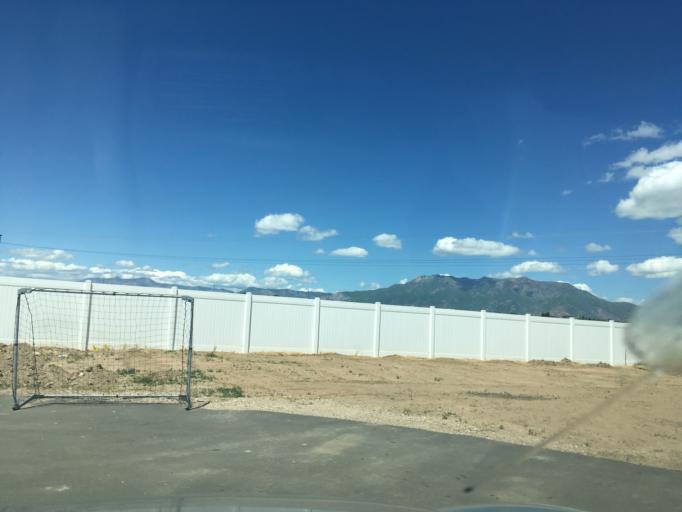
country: US
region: Utah
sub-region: Davis County
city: Layton
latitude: 41.0623
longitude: -112.0111
